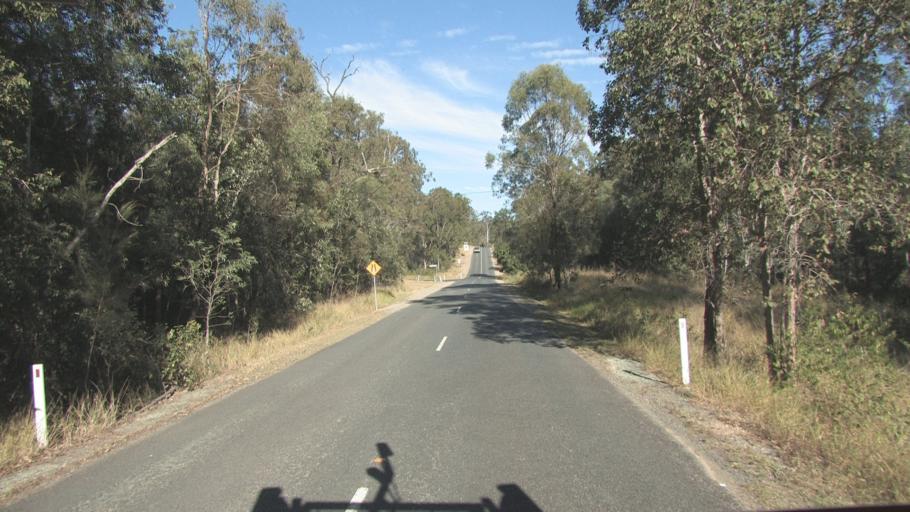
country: AU
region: Queensland
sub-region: Logan
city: Windaroo
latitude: -27.8136
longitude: 153.1682
